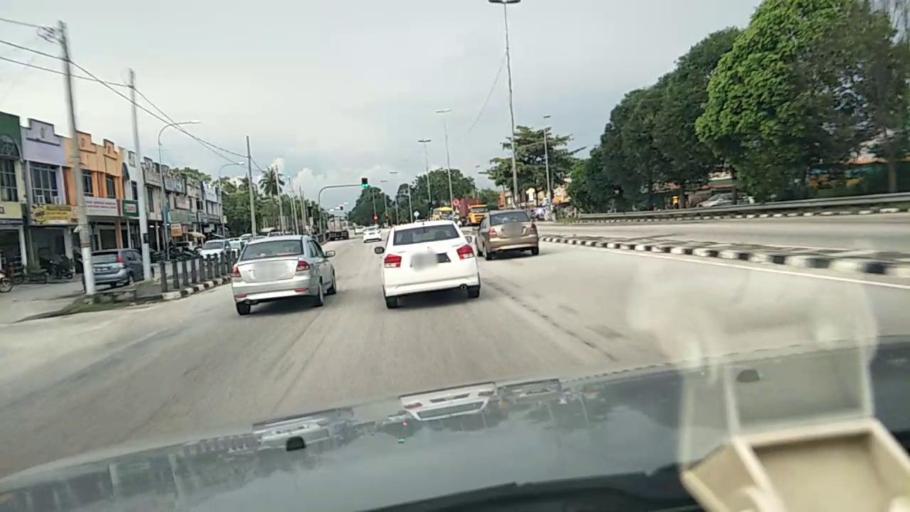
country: MY
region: Perak
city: Kampong Dungun
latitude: 3.1314
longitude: 101.3754
